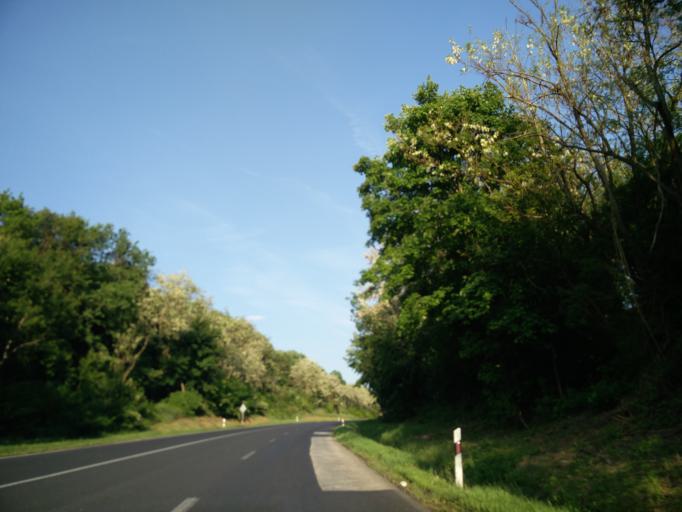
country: HU
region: Veszprem
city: Ajka
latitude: 47.1433
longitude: 17.5652
